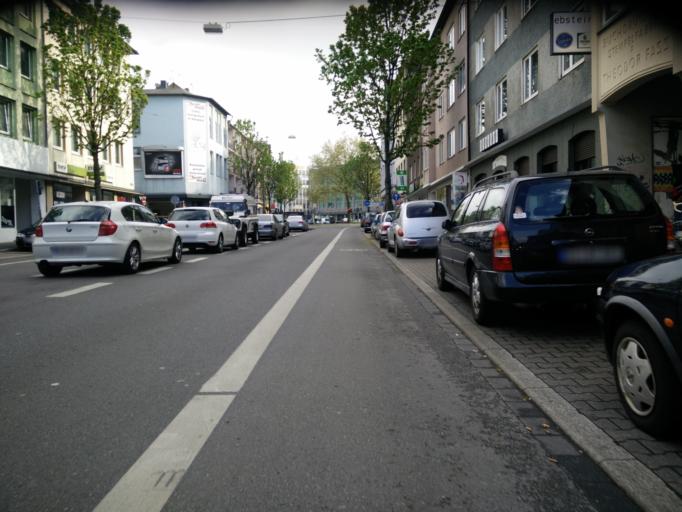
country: DE
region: North Rhine-Westphalia
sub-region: Regierungsbezirk Arnsberg
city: Bochum
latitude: 51.4868
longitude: 7.2142
